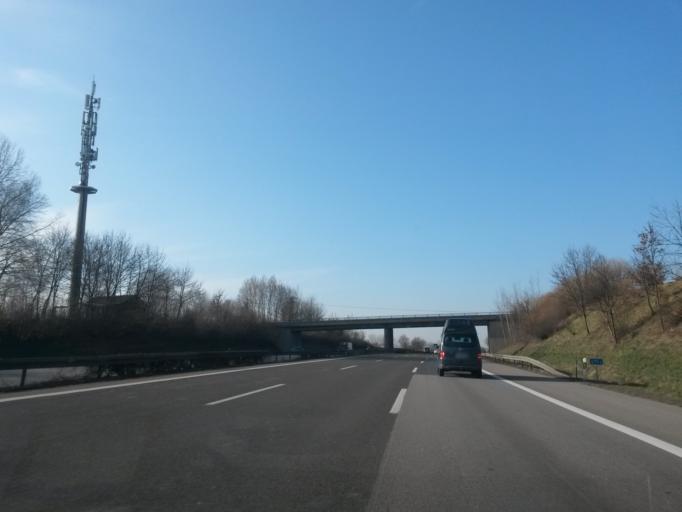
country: DE
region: Bavaria
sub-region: Upper Bavaria
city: Rohrbach
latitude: 48.6214
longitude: 11.5275
